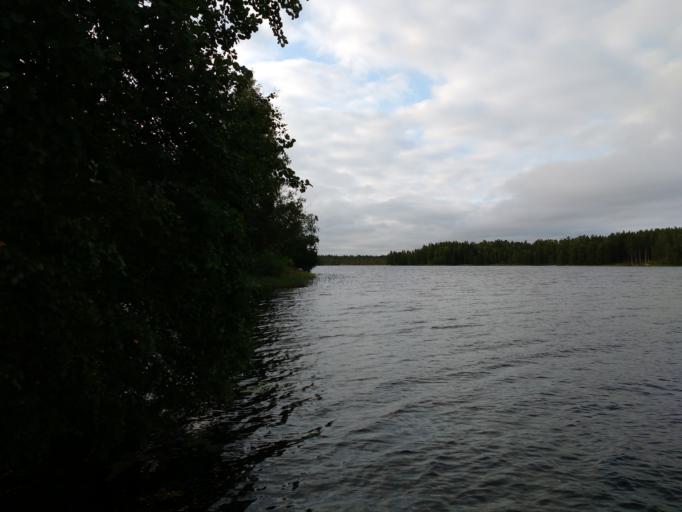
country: FI
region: Pirkanmaa
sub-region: Ylae-Pirkanmaa
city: Juupajoki
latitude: 61.8463
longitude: 24.2835
